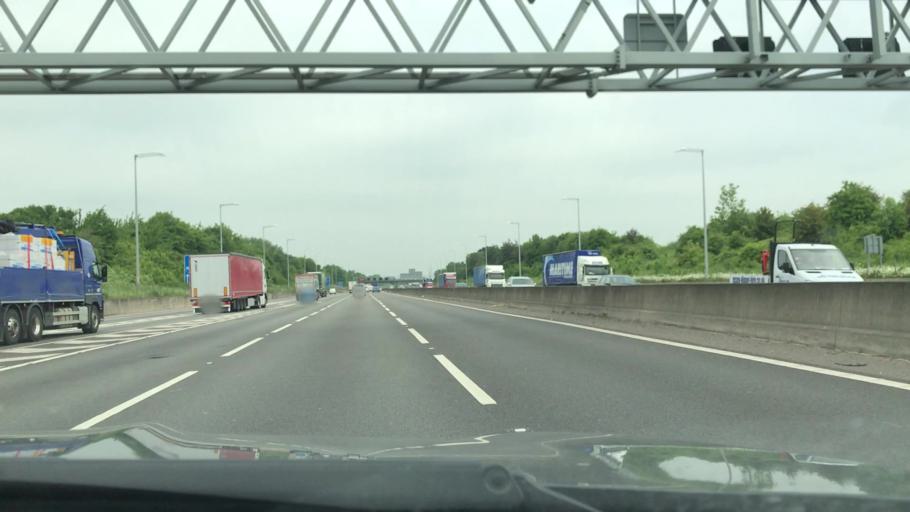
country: GB
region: England
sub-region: Essex
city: Aveley
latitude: 51.5008
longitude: 0.2682
